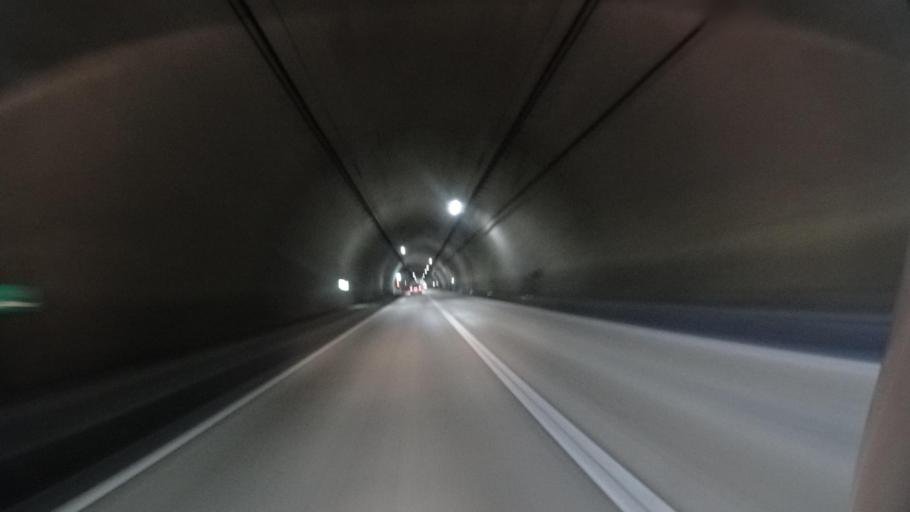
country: JP
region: Kyoto
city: Kameoka
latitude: 35.2265
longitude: 135.5732
